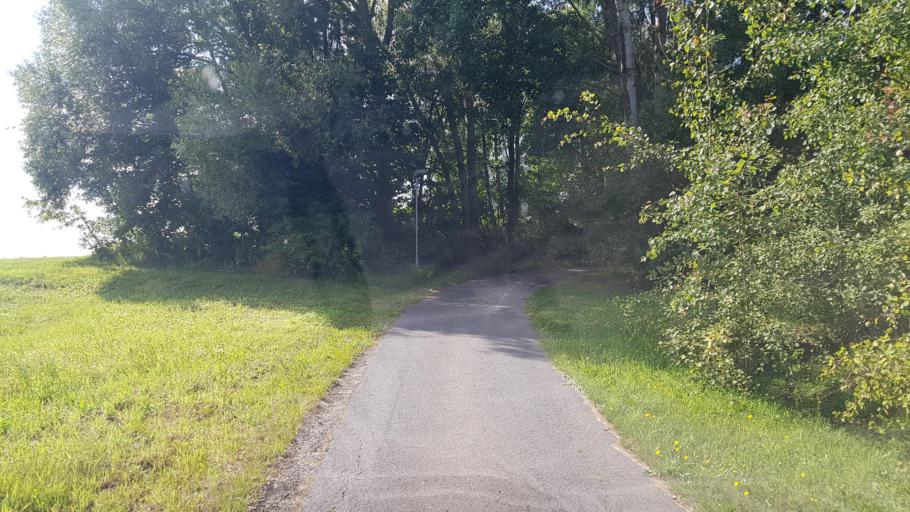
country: DE
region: Brandenburg
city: Sonnewalde
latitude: 51.7490
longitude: 13.6938
